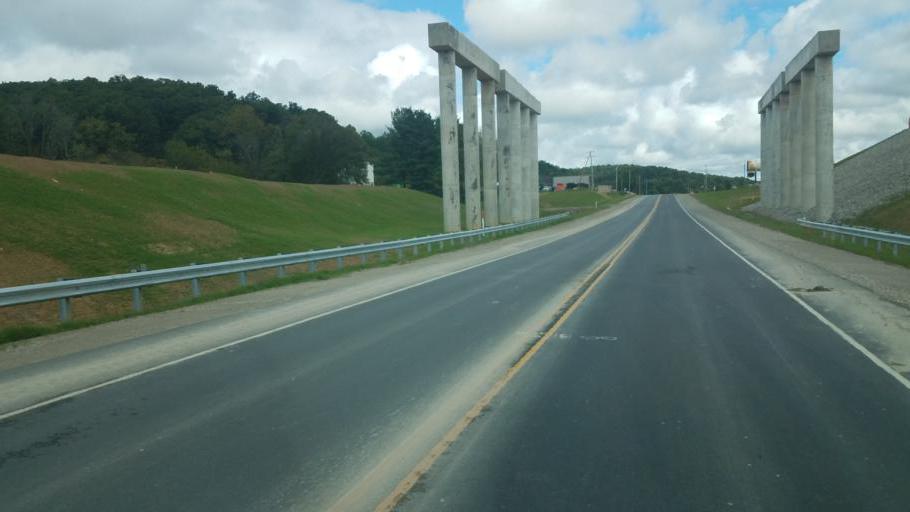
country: US
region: Ohio
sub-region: Scioto County
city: Lucasville
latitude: 38.8631
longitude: -82.8970
